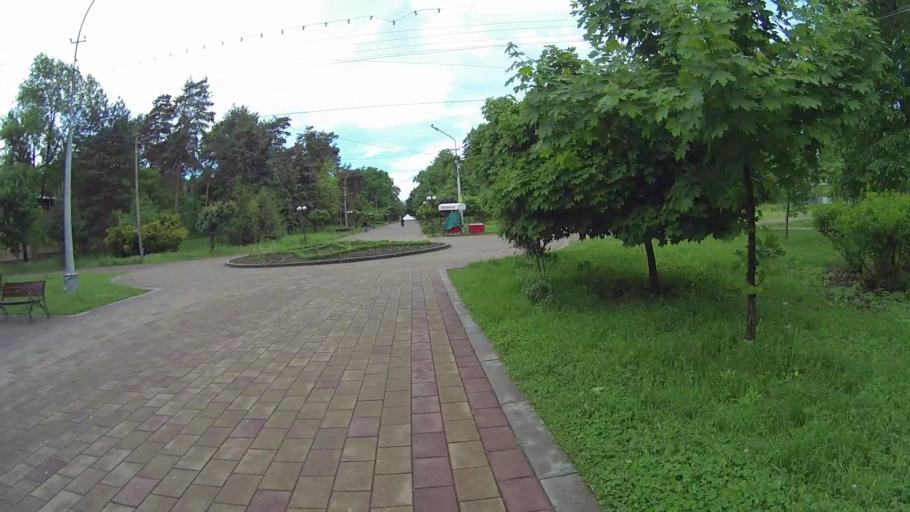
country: RU
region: Kabardino-Balkariya
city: Vol'nyy Aul
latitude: 43.4746
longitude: 43.6016
